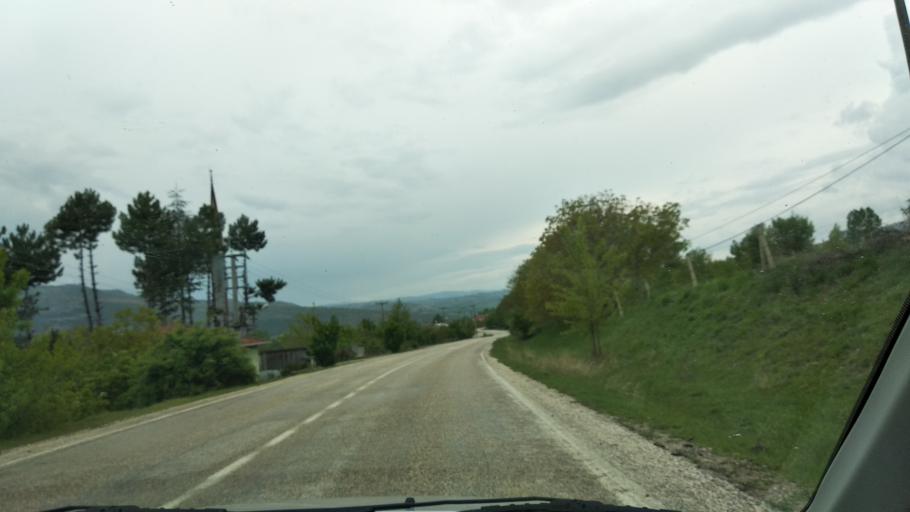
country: TR
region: Bolu
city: Seben
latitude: 40.4198
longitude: 31.5838
